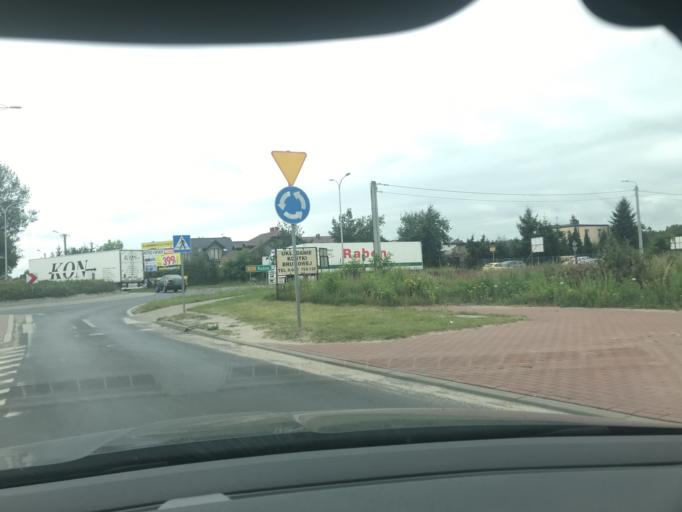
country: PL
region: Lodz Voivodeship
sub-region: Powiat zgierski
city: Zgierz
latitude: 51.8723
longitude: 19.4087
